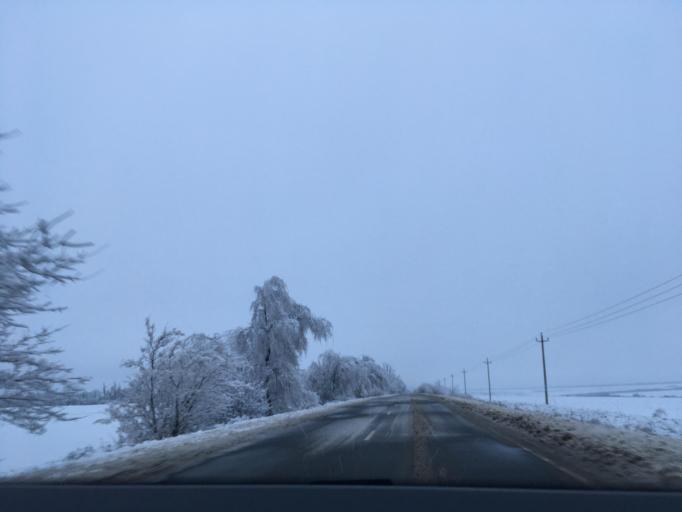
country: RU
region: Voronezj
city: Verkhniy Mamon
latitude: 50.0232
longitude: 40.0813
